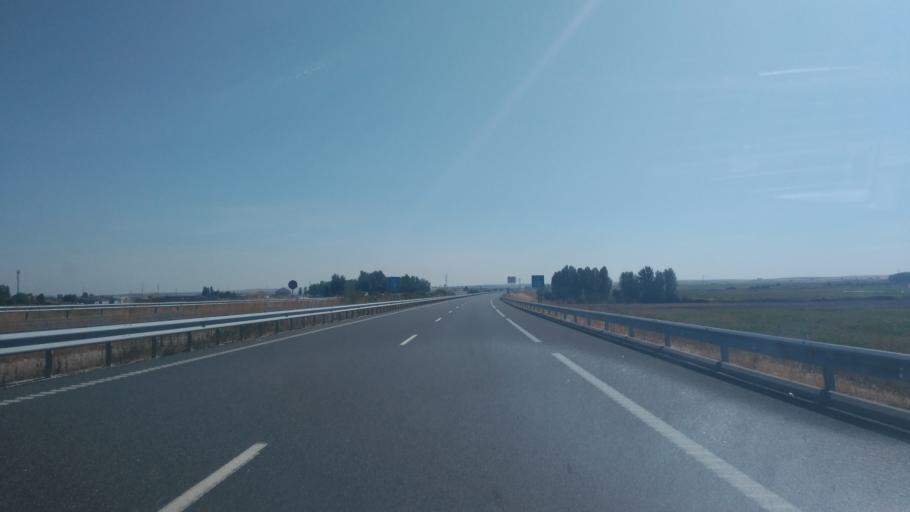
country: ES
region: Castille and Leon
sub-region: Provincia de Salamanca
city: Encinas de Abajo
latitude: 40.9284
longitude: -5.4788
